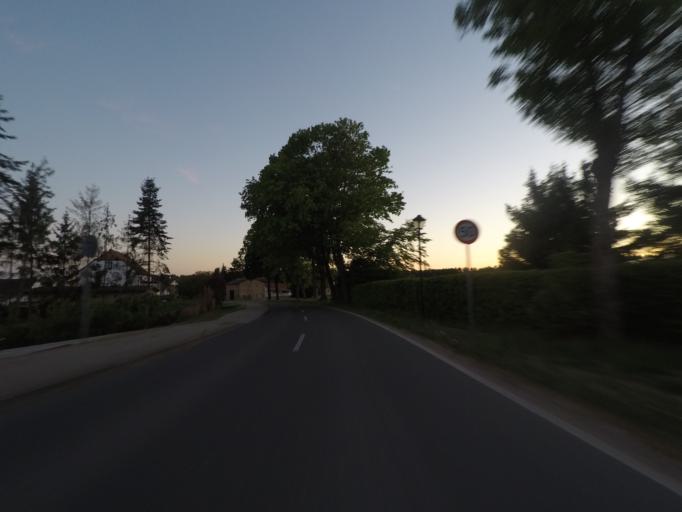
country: DE
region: Brandenburg
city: Marienwerder
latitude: 52.8579
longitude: 13.6822
